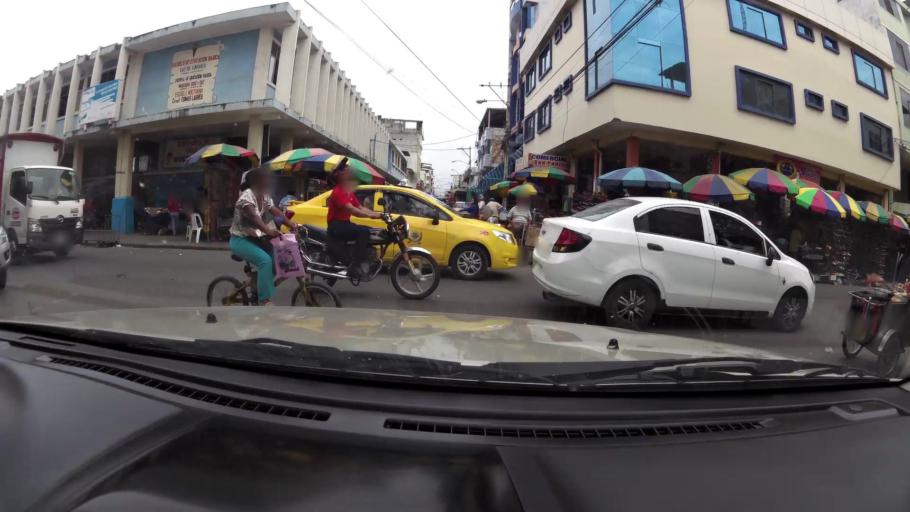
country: EC
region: El Oro
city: Machala
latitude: -3.2572
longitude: -79.9587
